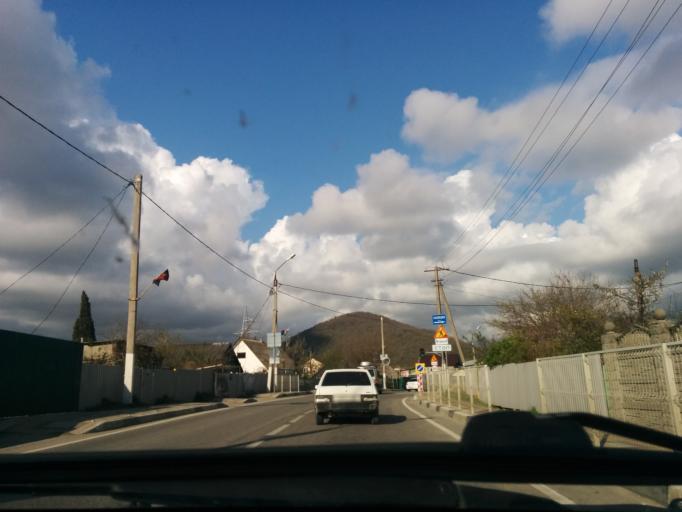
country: RU
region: Krasnodarskiy
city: Novomikhaylovskiy
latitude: 44.2576
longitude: 38.8572
